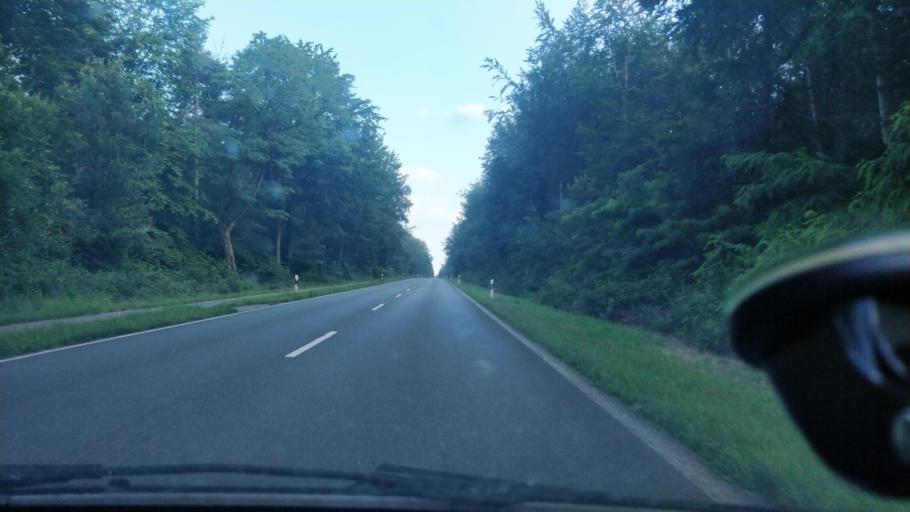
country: DE
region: North Rhine-Westphalia
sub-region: Regierungsbezirk Dusseldorf
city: Alpen
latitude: 51.5600
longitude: 6.4982
